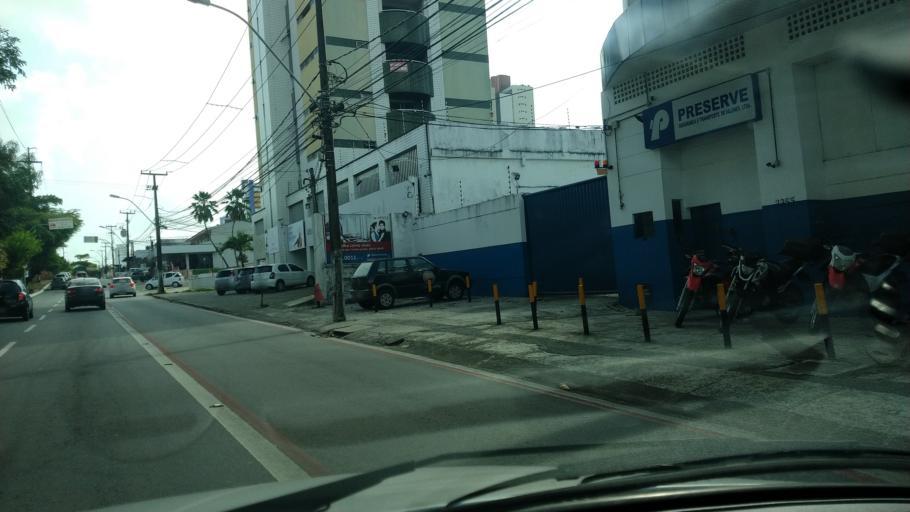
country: BR
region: Rio Grande do Norte
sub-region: Natal
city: Natal
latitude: -5.8026
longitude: -35.2067
